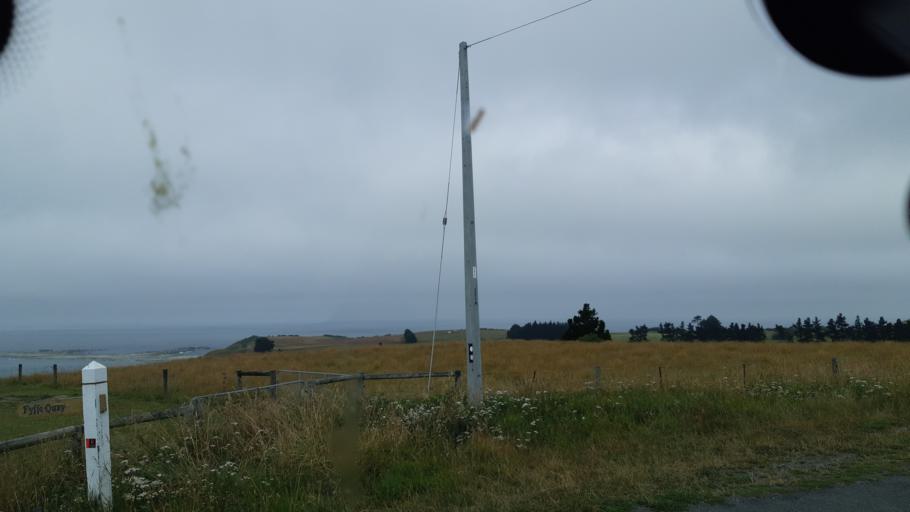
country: NZ
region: Canterbury
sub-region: Kaikoura District
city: Kaikoura
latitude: -42.4185
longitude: 173.7000
